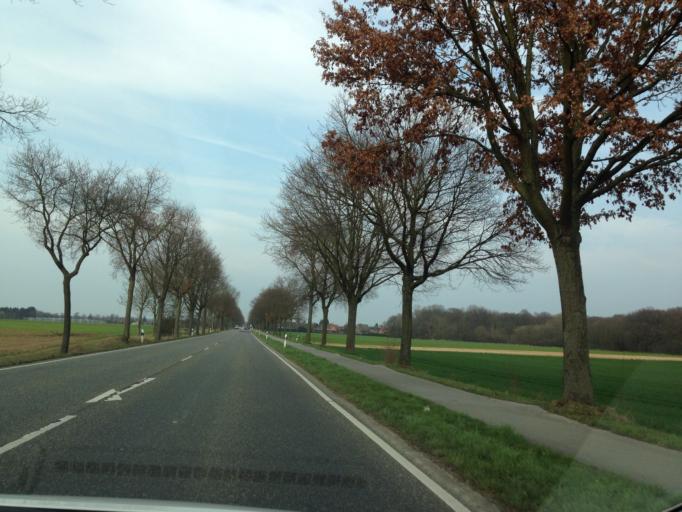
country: DE
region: North Rhine-Westphalia
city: Erkelenz
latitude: 51.0480
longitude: 6.2859
